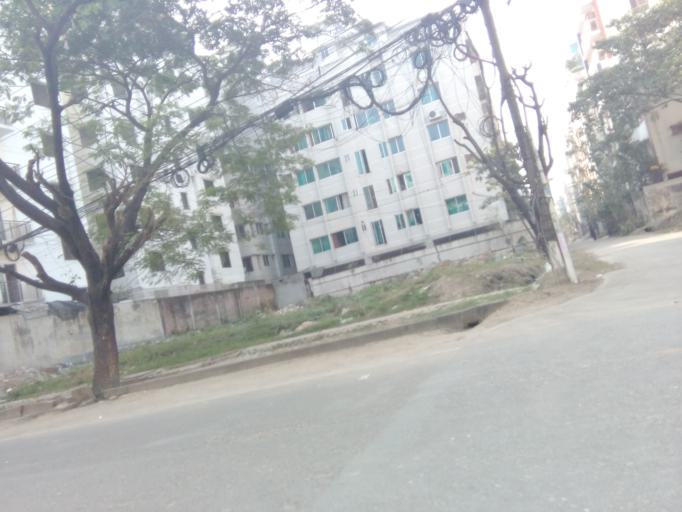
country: BD
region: Dhaka
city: Paltan
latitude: 23.8153
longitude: 90.4342
